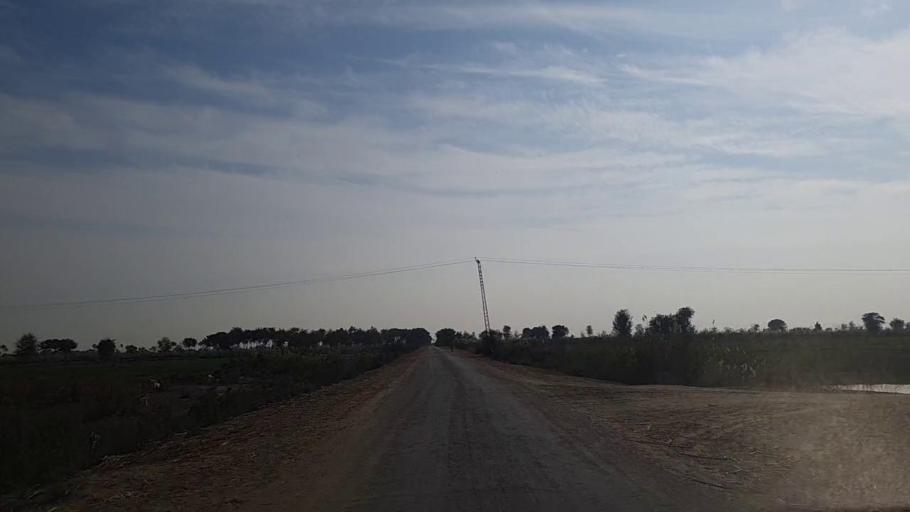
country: PK
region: Sindh
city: Daur
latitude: 26.4662
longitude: 68.4176
